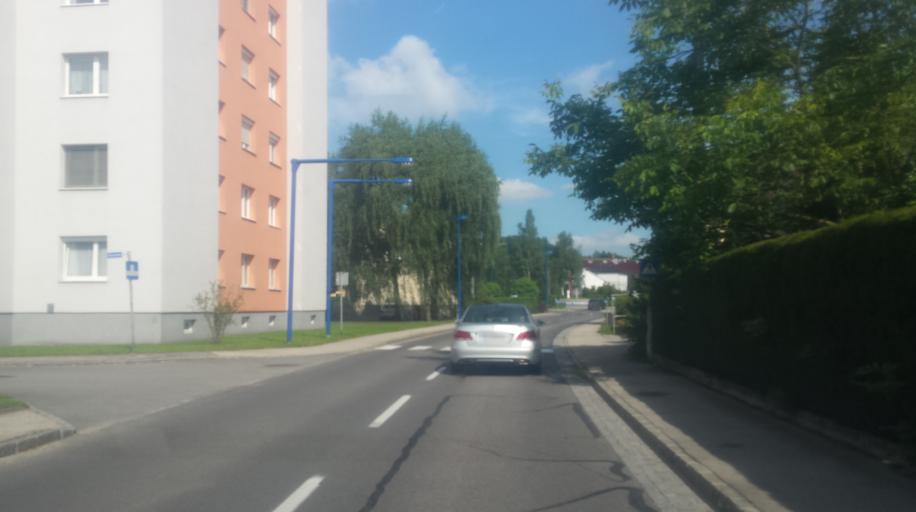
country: AT
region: Upper Austria
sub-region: Politischer Bezirk Grieskirchen
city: Bad Schallerbach
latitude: 48.2257
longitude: 13.9275
